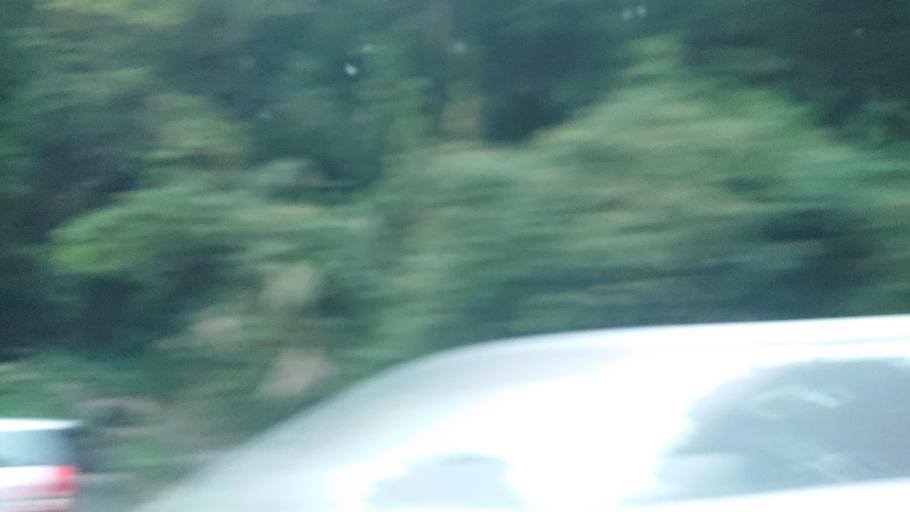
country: TW
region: Taiwan
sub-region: Chiayi
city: Jiayi Shi
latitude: 23.5059
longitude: 120.6938
